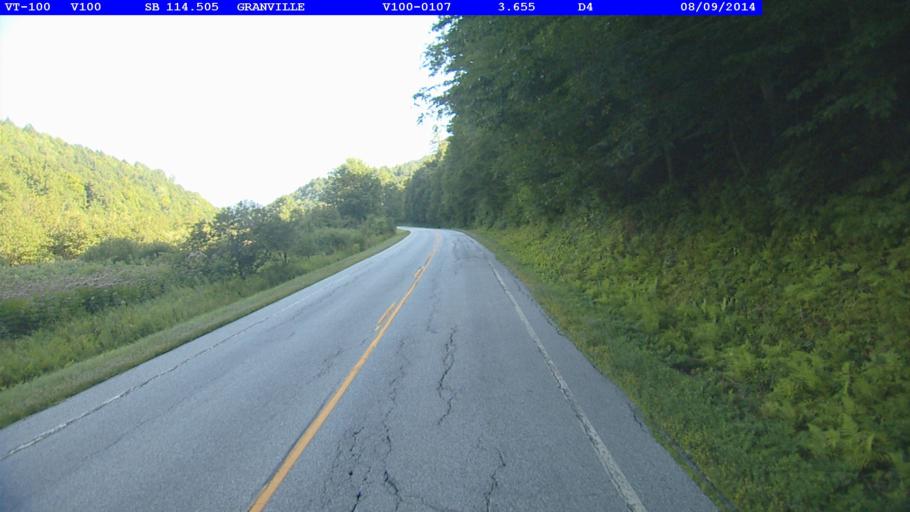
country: US
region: Vermont
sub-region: Orange County
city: Randolph
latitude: 43.9939
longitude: -72.8527
